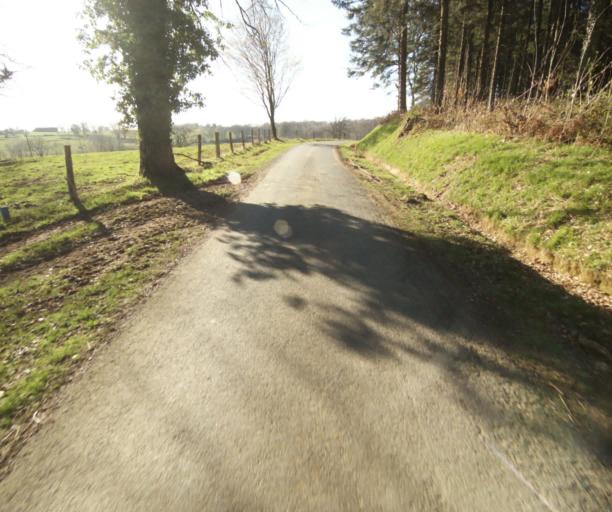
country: FR
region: Limousin
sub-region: Departement de la Correze
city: Seilhac
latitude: 45.3849
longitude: 1.6968
